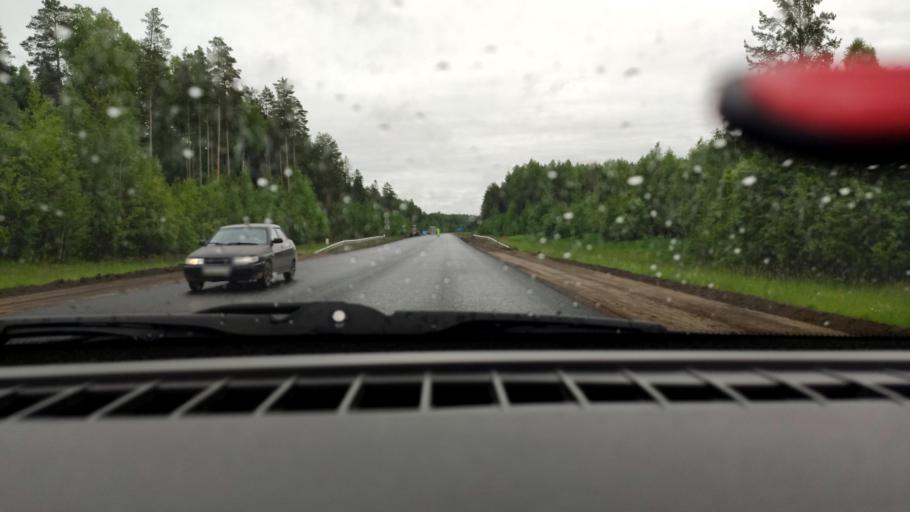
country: RU
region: Perm
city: Karagay
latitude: 58.2460
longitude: 54.9354
